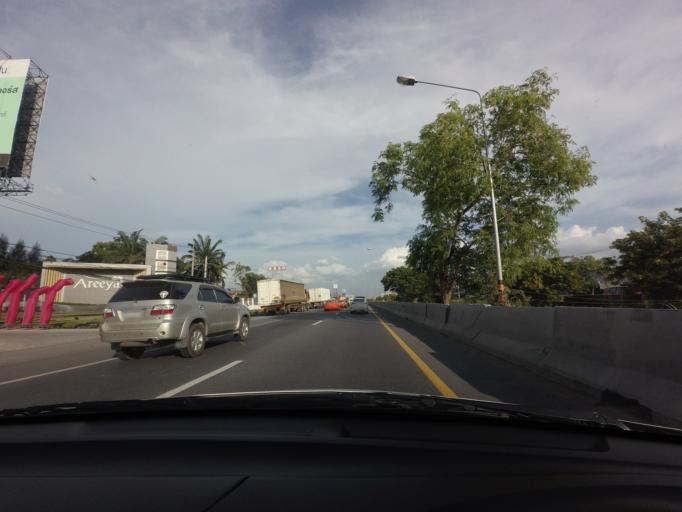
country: TH
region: Pathum Thani
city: Lat Lum Kaeo
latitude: 13.9769
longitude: 100.3911
